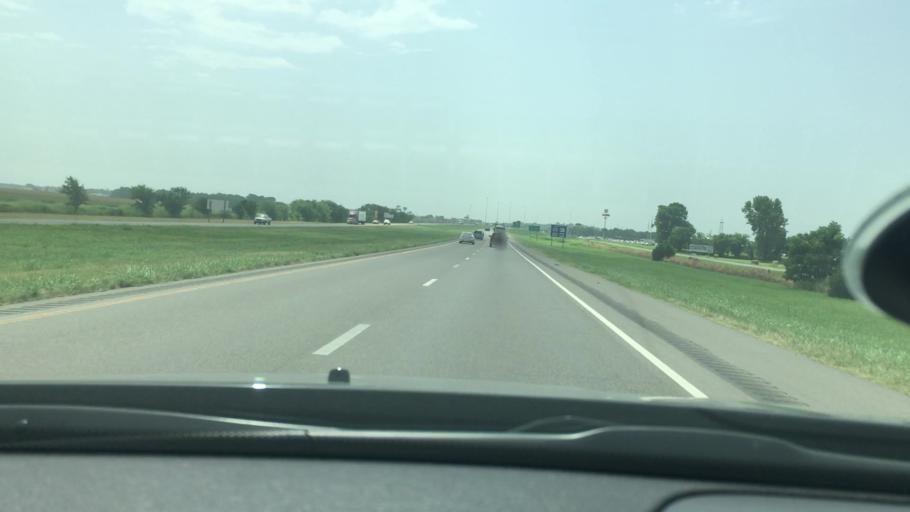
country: US
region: Oklahoma
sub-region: Garvin County
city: Pauls Valley
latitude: 34.7490
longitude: -97.2730
